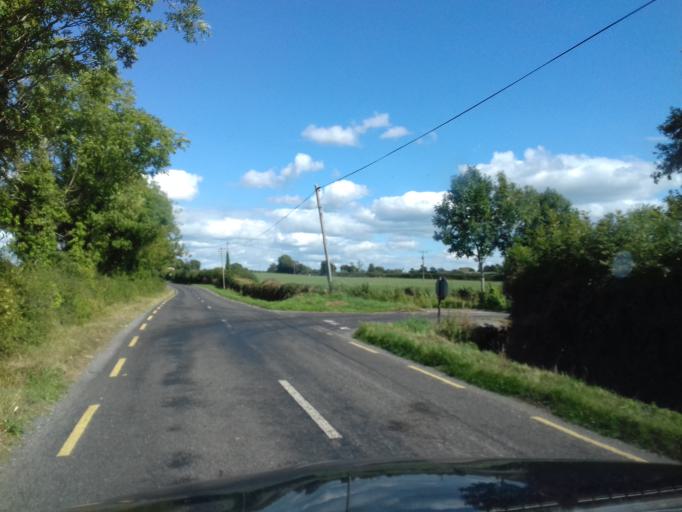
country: IE
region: Leinster
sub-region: Kilkenny
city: Callan
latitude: 52.5339
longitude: -7.3590
